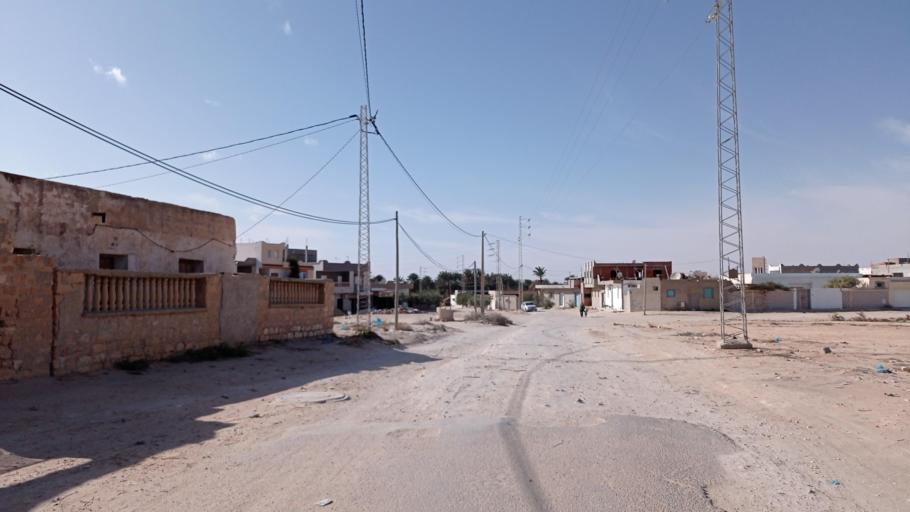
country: TN
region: Qabis
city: Gabes
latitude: 33.8374
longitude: 10.1155
